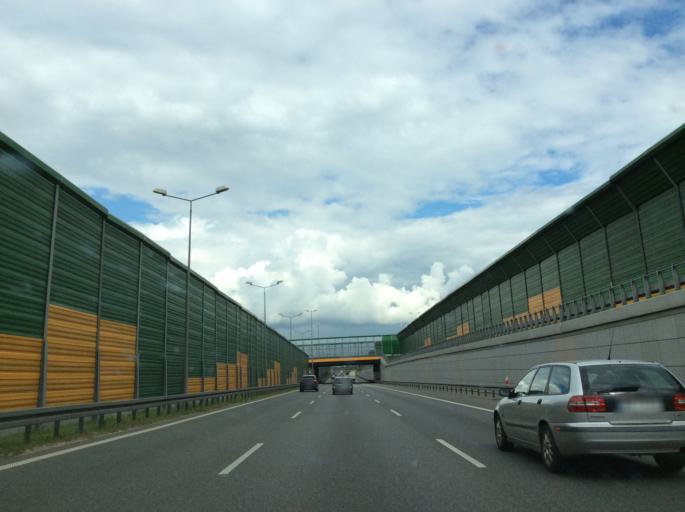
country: PL
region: Masovian Voivodeship
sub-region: Warszawa
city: Bemowo
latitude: 52.2454
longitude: 20.9089
